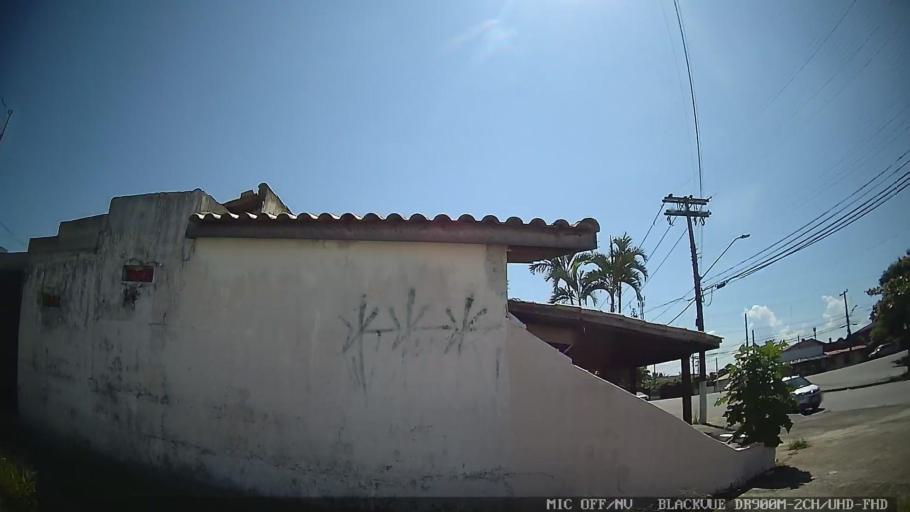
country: BR
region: Sao Paulo
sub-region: Peruibe
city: Peruibe
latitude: -24.3060
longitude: -46.9798
